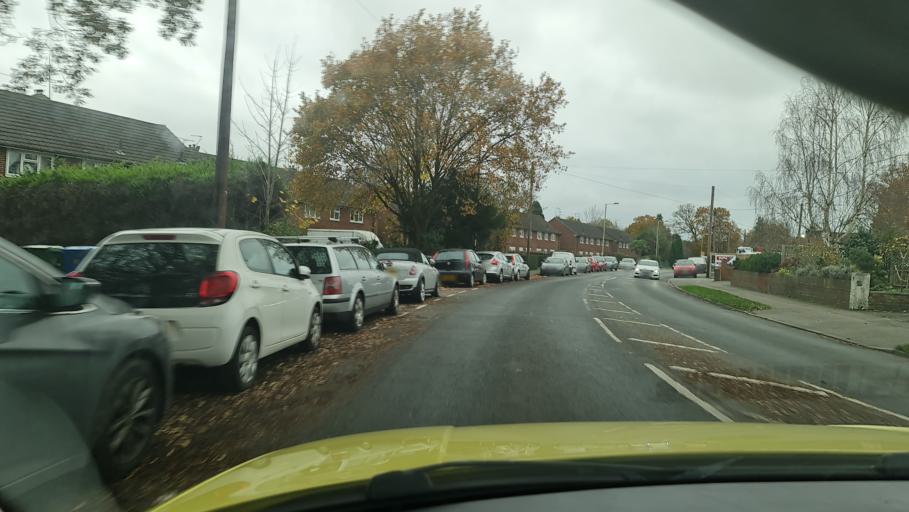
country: GB
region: England
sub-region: Surrey
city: Frimley
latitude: 51.3141
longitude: -0.7676
